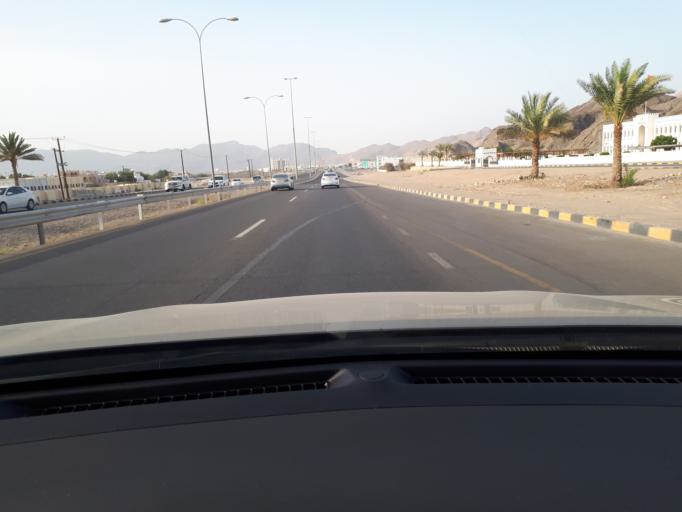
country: OM
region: Muhafazat Masqat
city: Bawshar
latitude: 23.4737
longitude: 58.4955
